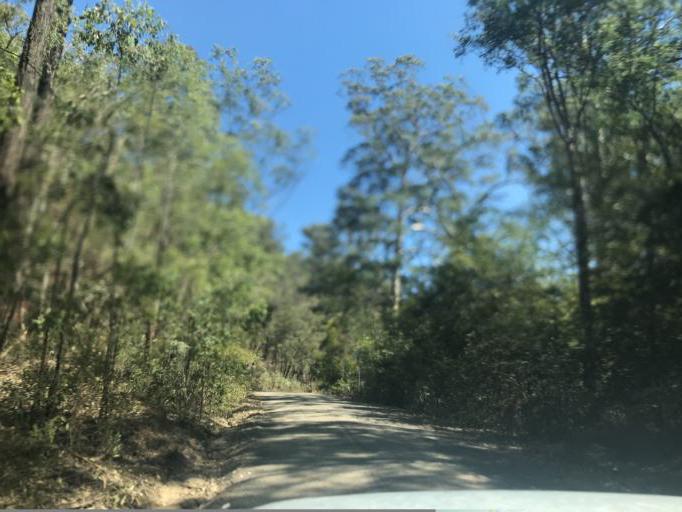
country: AU
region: New South Wales
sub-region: Wyong Shire
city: Little Jilliby
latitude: -33.1868
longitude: 151.0554
